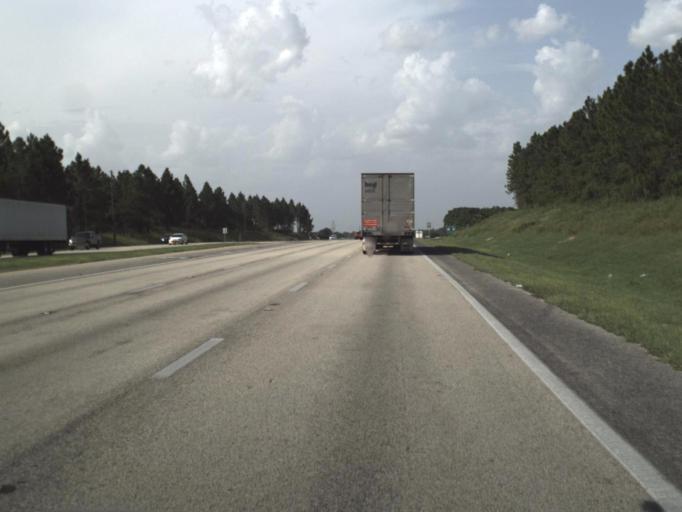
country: US
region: Florida
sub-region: Polk County
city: Haines City
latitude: 28.0915
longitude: -81.6483
